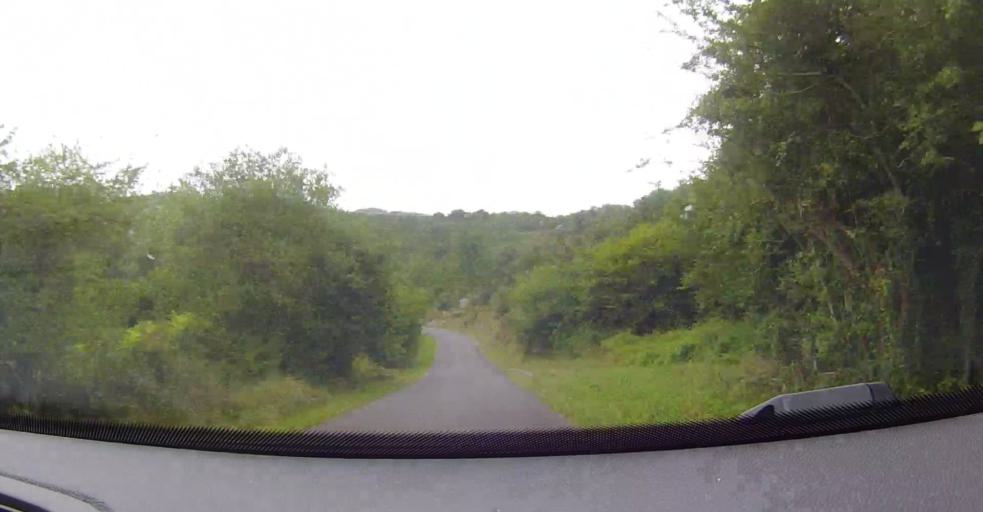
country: ES
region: Cantabria
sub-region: Provincia de Cantabria
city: Rasines
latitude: 43.2637
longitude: -3.3770
